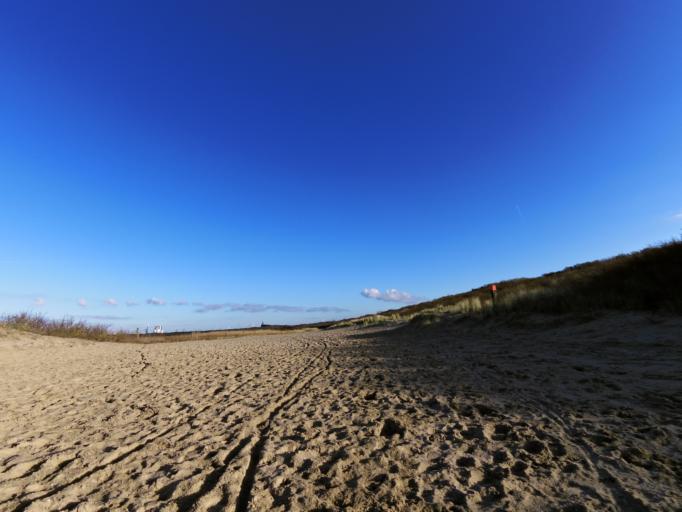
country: NL
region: South Holland
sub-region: Gemeente Hellevoetsluis
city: Nieuw-Helvoet
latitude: 51.9103
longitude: 4.0540
